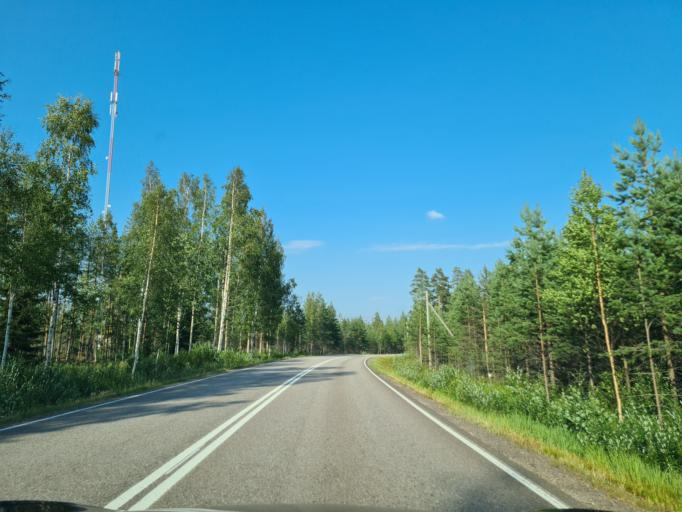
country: FI
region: Satakunta
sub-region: Pohjois-Satakunta
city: Karvia
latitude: 62.3223
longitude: 22.6726
